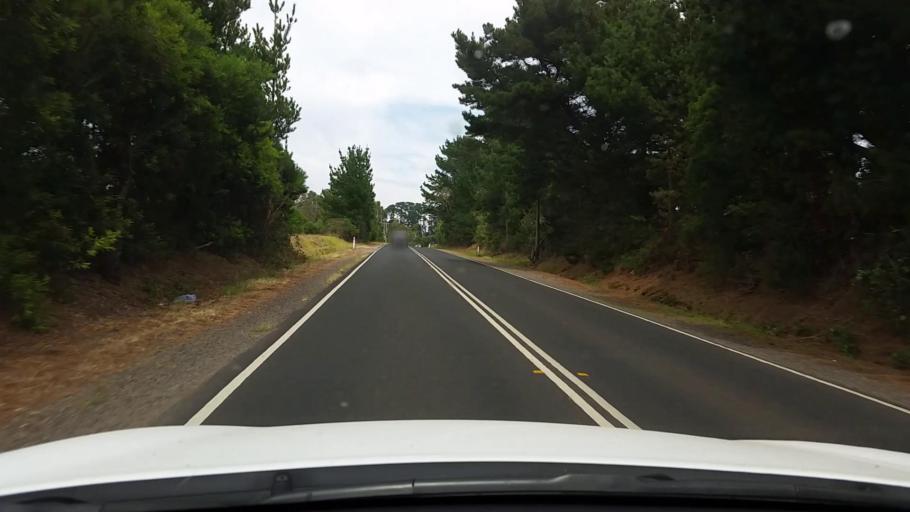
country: AU
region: Victoria
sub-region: Mornington Peninsula
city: Merricks
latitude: -38.4119
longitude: 145.0579
